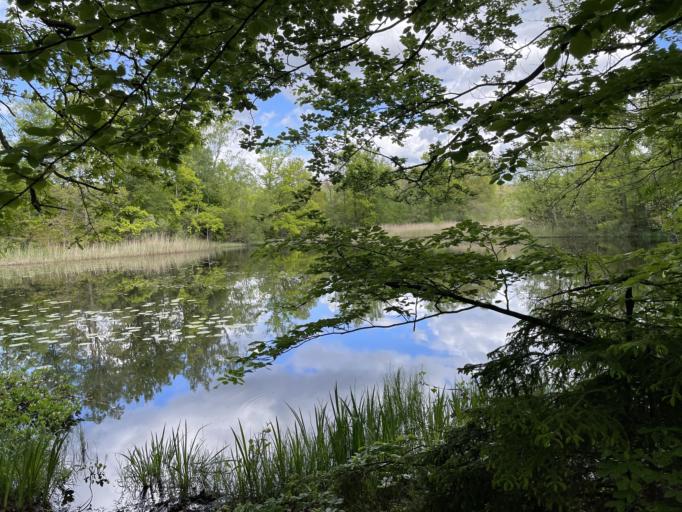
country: SE
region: Skane
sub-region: Klippans Kommun
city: Klippan
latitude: 56.1610
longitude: 13.1446
